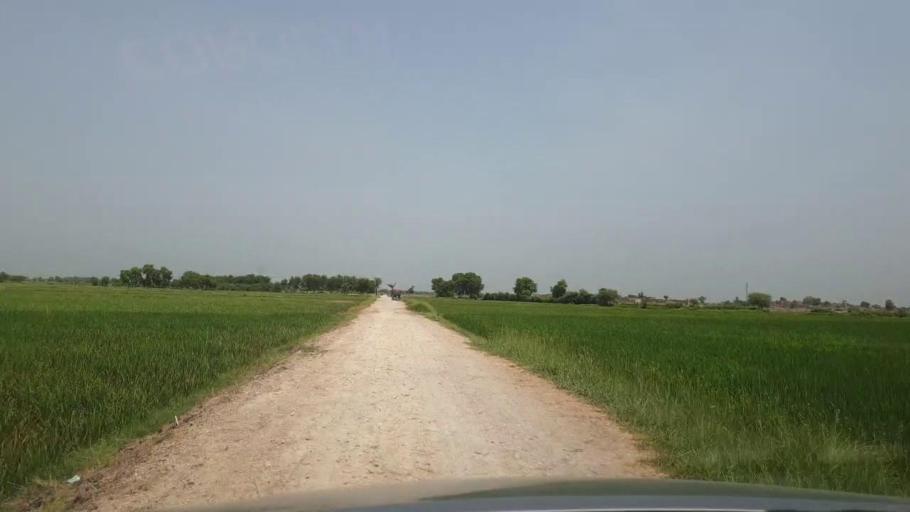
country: PK
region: Sindh
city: Madeji
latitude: 27.7568
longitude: 68.3731
